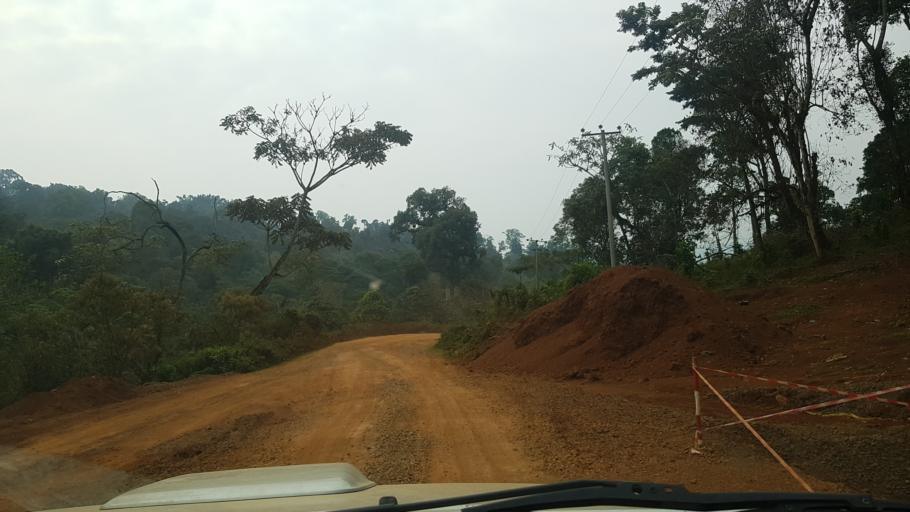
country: ET
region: Oromiya
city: Gore
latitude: 7.8800
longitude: 35.4842
